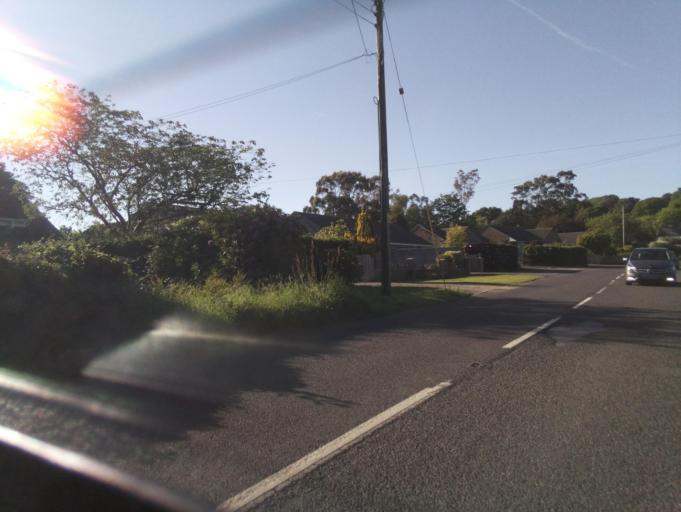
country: GB
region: England
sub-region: Dorset
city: Lyme Regis
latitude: 50.7980
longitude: -2.8679
